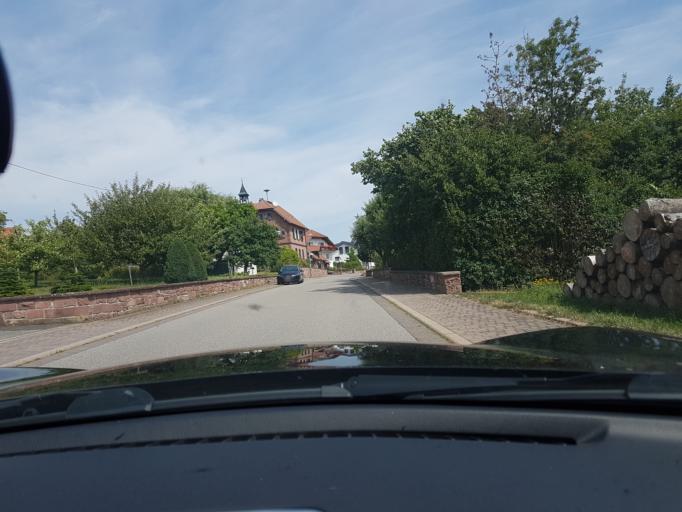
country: DE
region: Baden-Wuerttemberg
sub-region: Karlsruhe Region
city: Mudau
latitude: 49.5242
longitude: 9.1578
